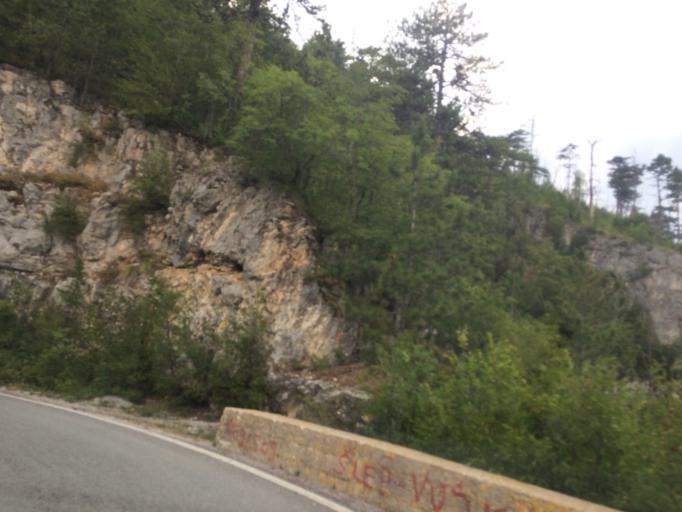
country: ME
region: Opstina Zabljak
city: Zabljak
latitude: 43.1607
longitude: 19.2618
